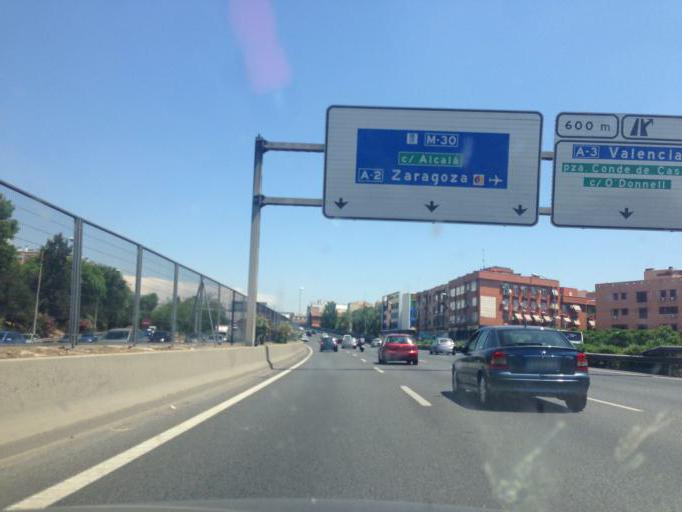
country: ES
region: Madrid
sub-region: Provincia de Madrid
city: Puente de Vallecas
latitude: 40.3951
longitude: -3.6725
